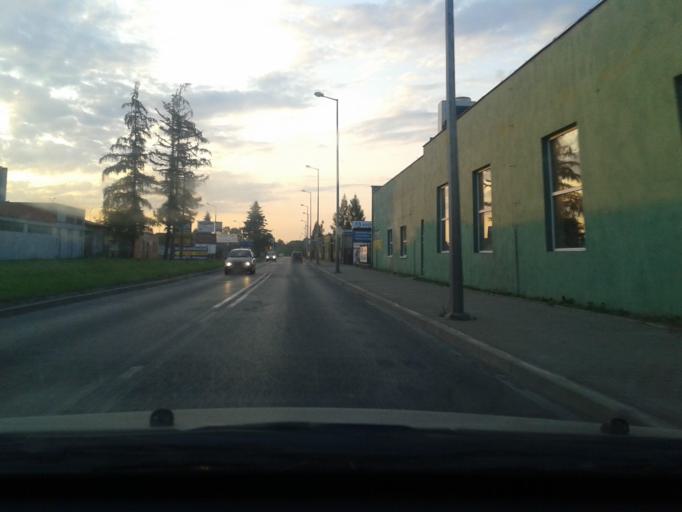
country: PL
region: Lesser Poland Voivodeship
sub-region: Powiat oswiecimski
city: Brzezinka
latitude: 50.0304
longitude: 19.1949
